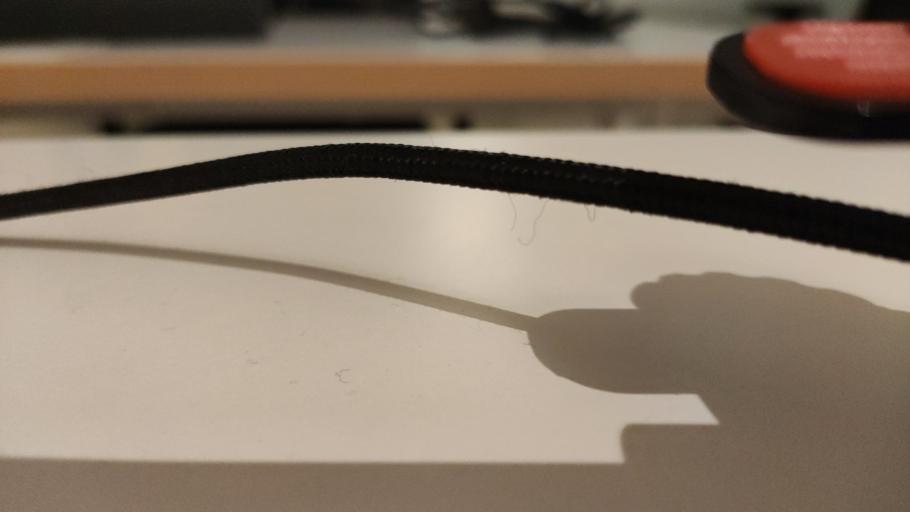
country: RU
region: Moskovskaya
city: Budenovetc
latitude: 56.3907
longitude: 37.6283
